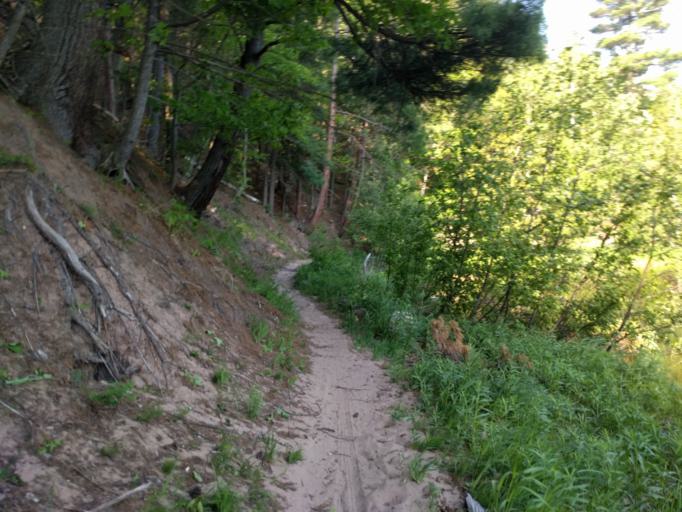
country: US
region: Michigan
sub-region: Marquette County
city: Trowbridge Park
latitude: 46.5688
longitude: -87.4465
